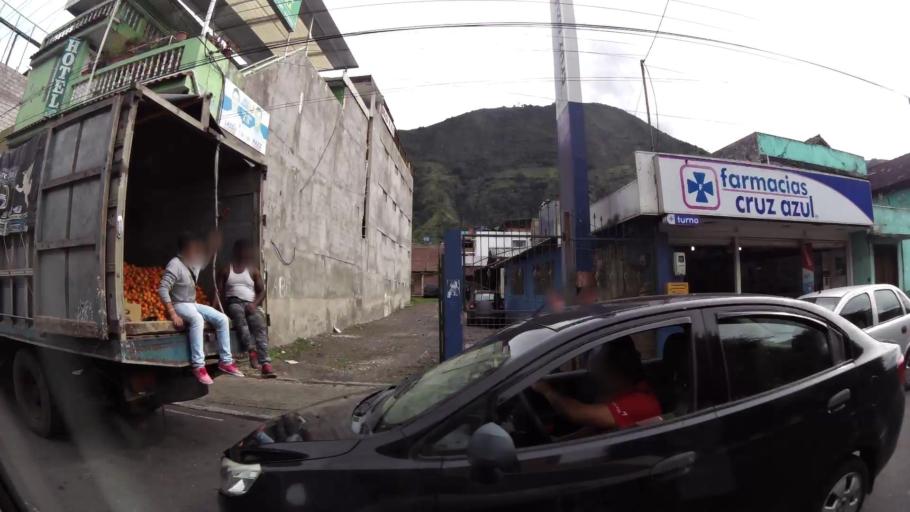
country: EC
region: Tungurahua
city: Banos
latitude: -1.3952
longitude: -78.4236
